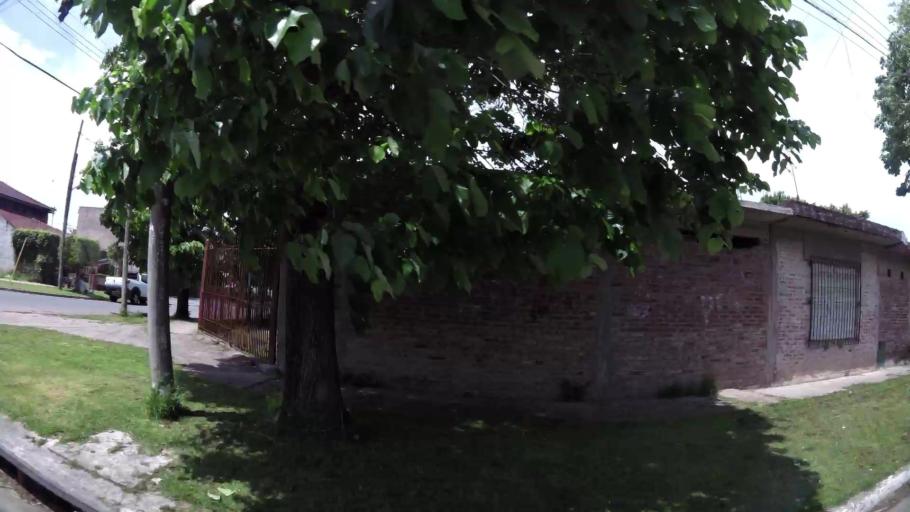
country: AR
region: Buenos Aires
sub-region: Partido de Quilmes
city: Quilmes
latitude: -34.7759
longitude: -58.2585
